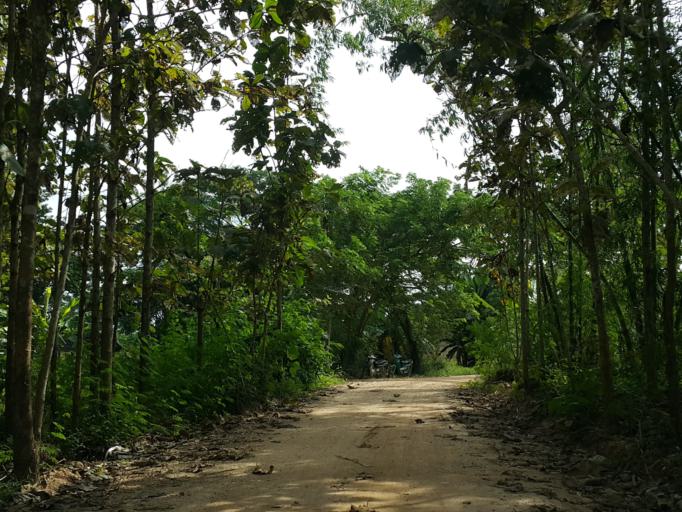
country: TH
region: Lampang
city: Hang Chat
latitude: 18.4821
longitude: 99.4035
